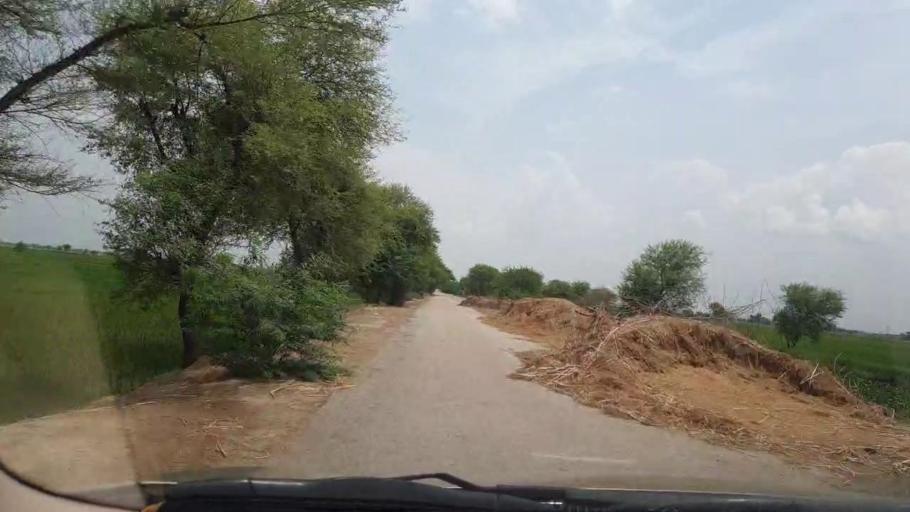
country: PK
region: Sindh
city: Larkana
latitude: 27.6083
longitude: 68.1515
